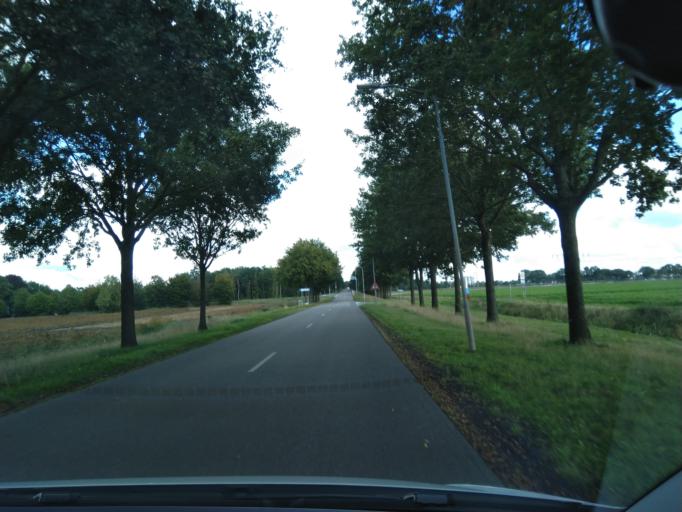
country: NL
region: Groningen
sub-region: Gemeente Veendam
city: Veendam
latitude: 53.0899
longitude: 6.9087
